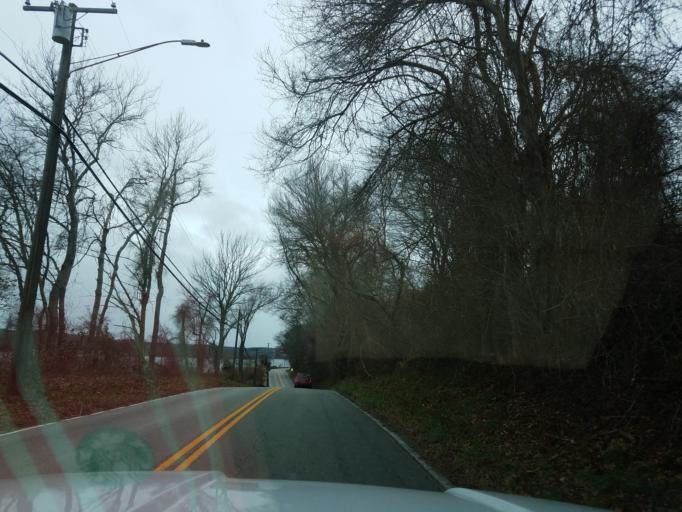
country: US
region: Connecticut
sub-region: New London County
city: Conning Towers-Nautilus Park
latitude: 41.3757
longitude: -72.0862
